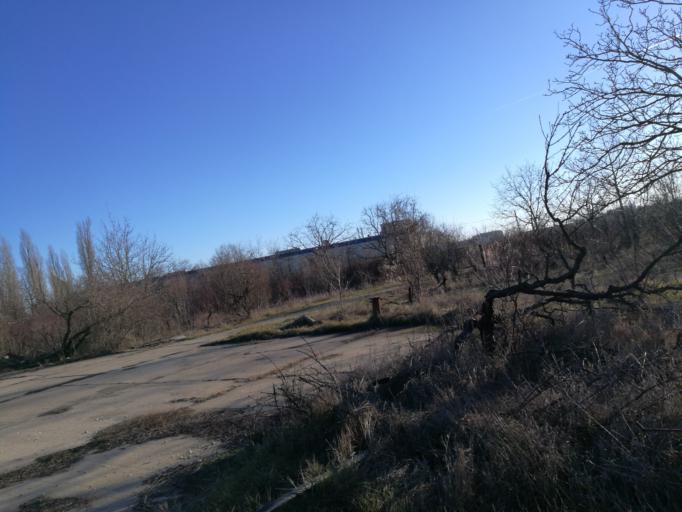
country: RO
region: Ilfov
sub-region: Comuna Otopeni
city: Otopeni
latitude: 44.5047
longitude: 26.0774
